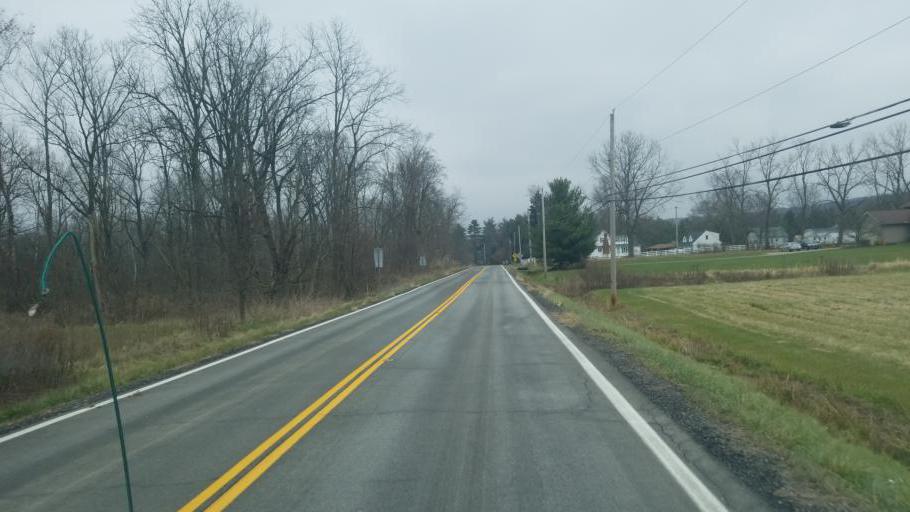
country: US
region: Ohio
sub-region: Cuyahoga County
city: North Royalton
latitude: 41.2402
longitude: -81.7259
